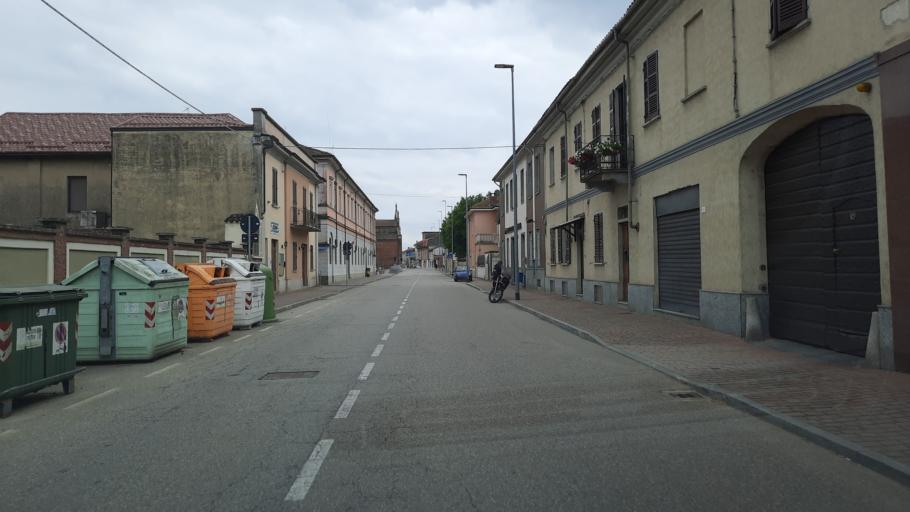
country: IT
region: Lombardy
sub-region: Provincia di Pavia
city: Palestro
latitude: 45.3033
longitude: 8.5330
